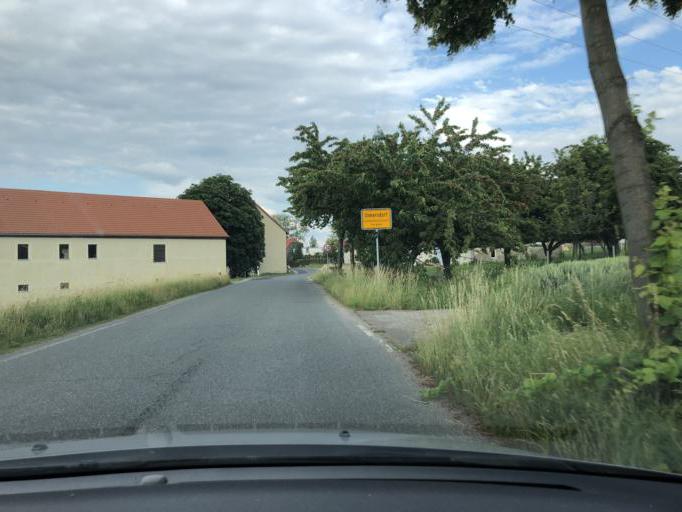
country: DE
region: Saxony
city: Wilsdruff
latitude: 51.0545
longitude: 13.5913
